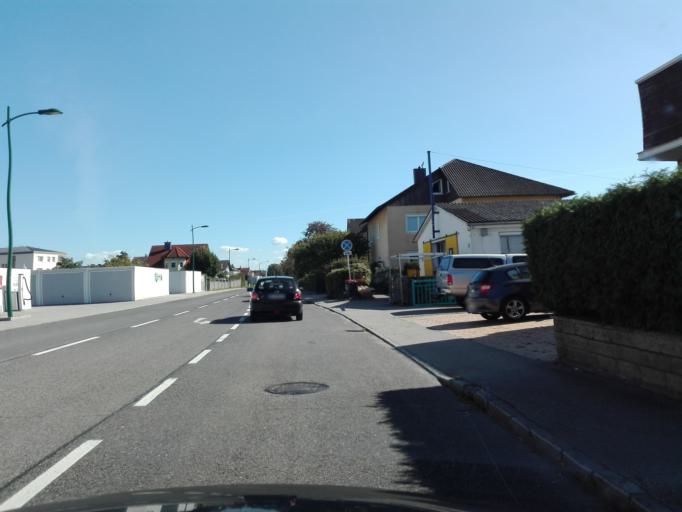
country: AT
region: Lower Austria
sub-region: Politischer Bezirk Amstetten
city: Ennsdorf
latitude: 48.2122
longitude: 14.4896
